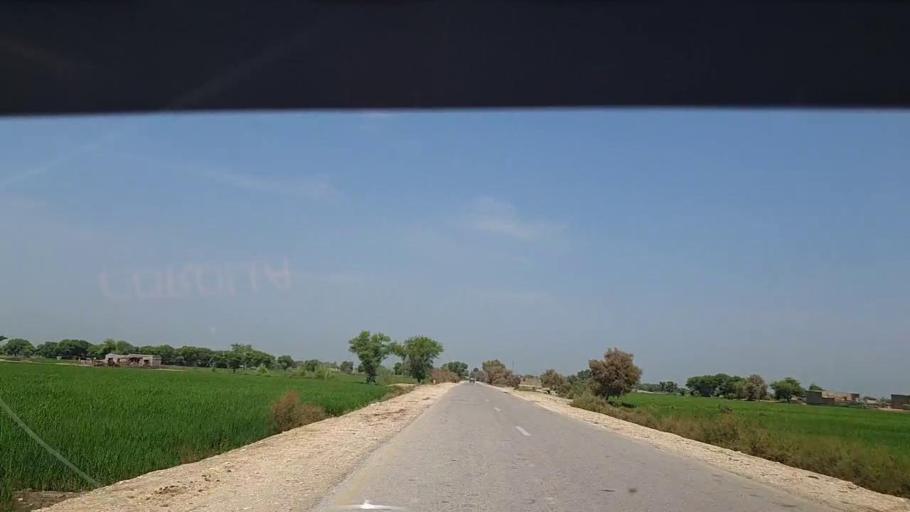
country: PK
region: Sindh
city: Thul
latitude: 28.1437
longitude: 68.8177
